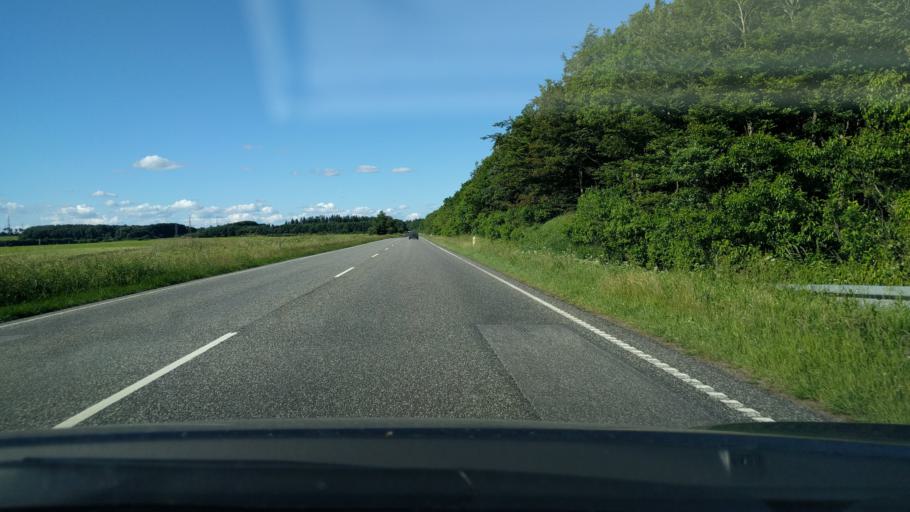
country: DK
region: North Denmark
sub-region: Vesthimmerland Kommune
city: Alestrup
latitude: 56.6261
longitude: 9.5137
